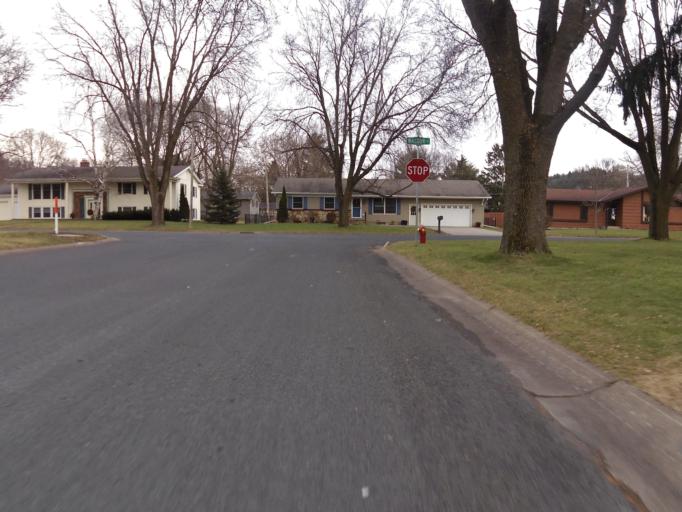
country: US
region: Wisconsin
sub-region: Pierce County
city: River Falls
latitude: 44.8577
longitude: -92.6110
